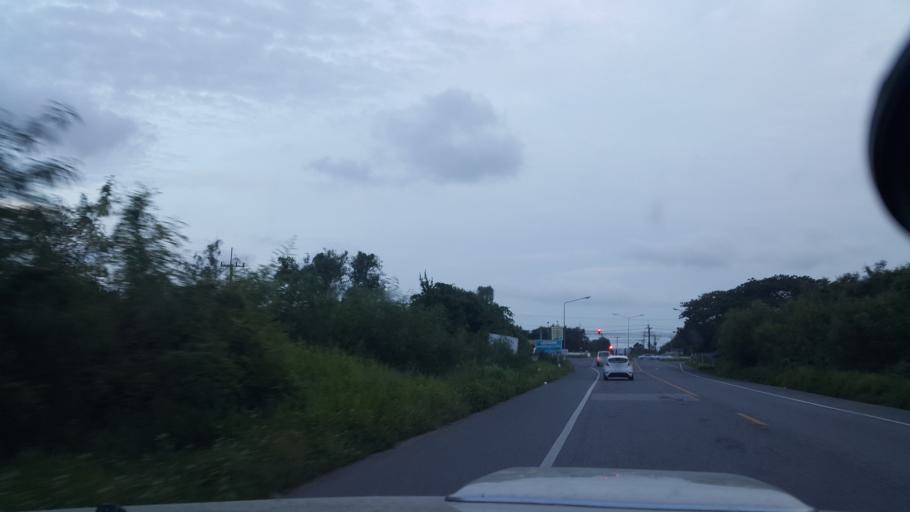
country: TH
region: Rayong
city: Ban Chang
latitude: 12.7045
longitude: 101.0098
